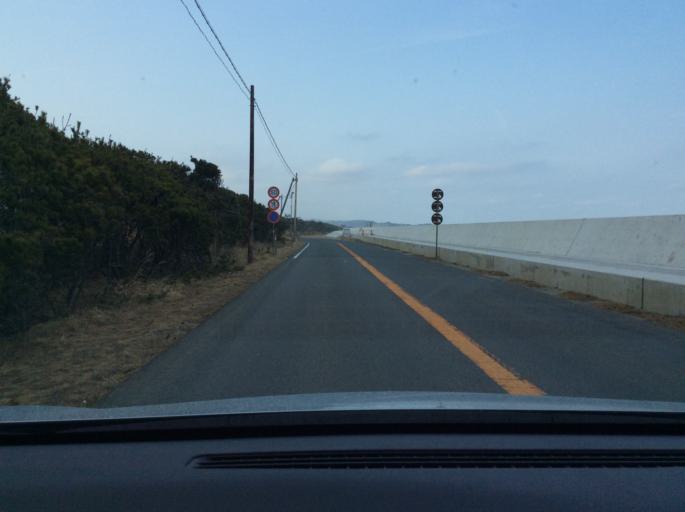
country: JP
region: Fukushima
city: Iwaki
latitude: 37.0642
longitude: 140.9756
